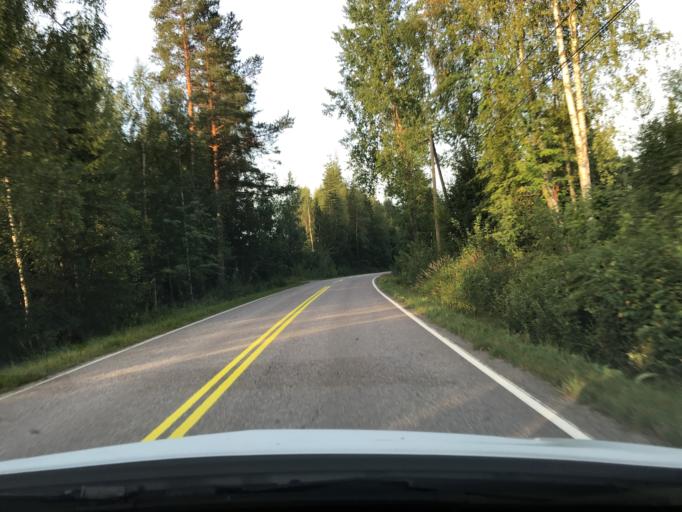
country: FI
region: Uusimaa
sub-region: Helsinki
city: Vihti
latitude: 60.4232
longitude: 24.5095
